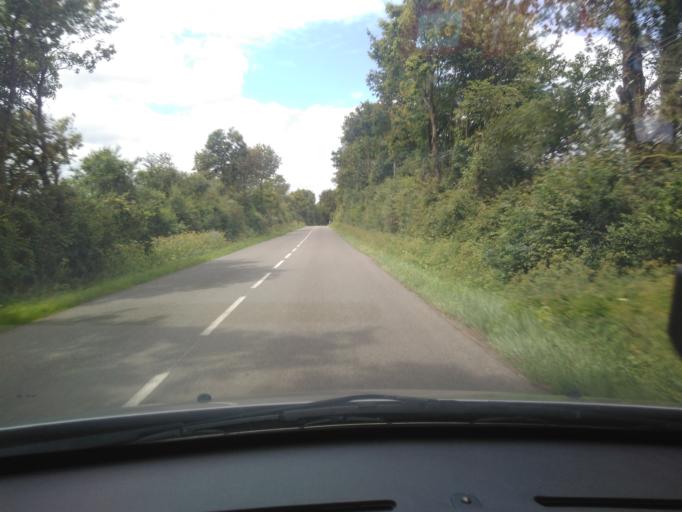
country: FR
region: Pays de la Loire
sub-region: Departement de la Vendee
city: Chauche
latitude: 46.7850
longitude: -1.2875
